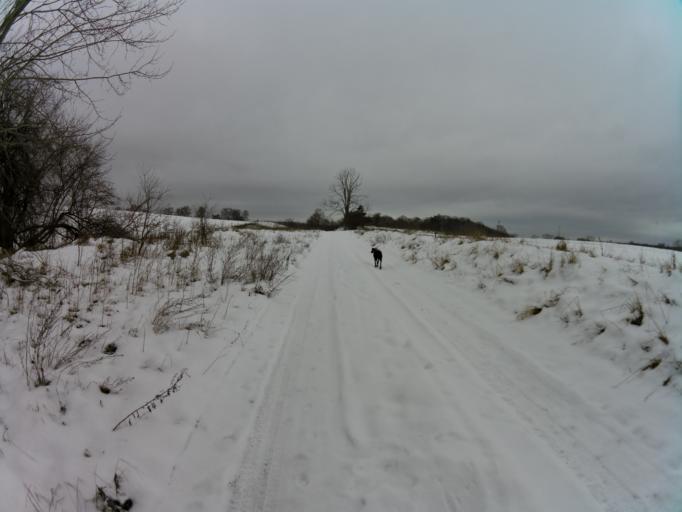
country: PL
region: West Pomeranian Voivodeship
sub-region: Powiat choszczenski
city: Recz
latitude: 53.3382
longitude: 15.5397
